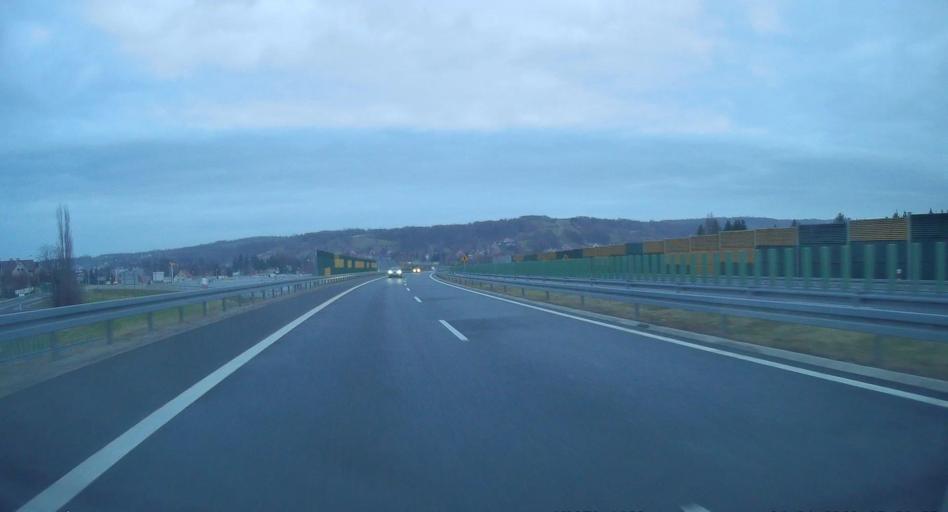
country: PL
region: Subcarpathian Voivodeship
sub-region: Powiat ropczycko-sedziszowski
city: Ropczyce
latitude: 50.0555
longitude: 21.5970
